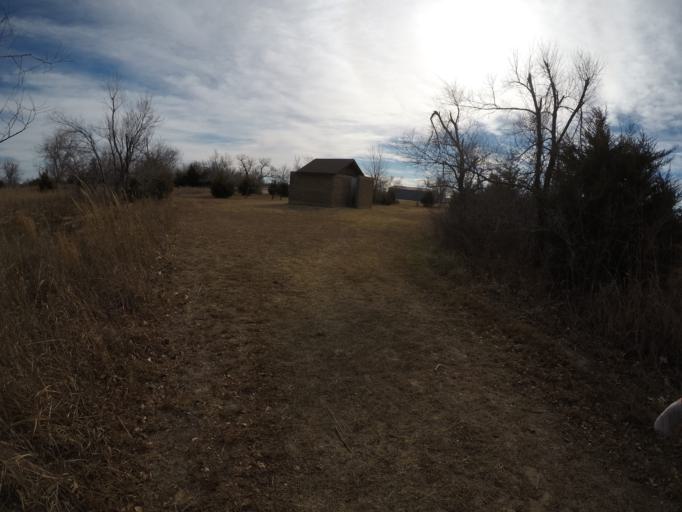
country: US
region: Kansas
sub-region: Reno County
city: Buhler
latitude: 38.1167
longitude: -97.8572
